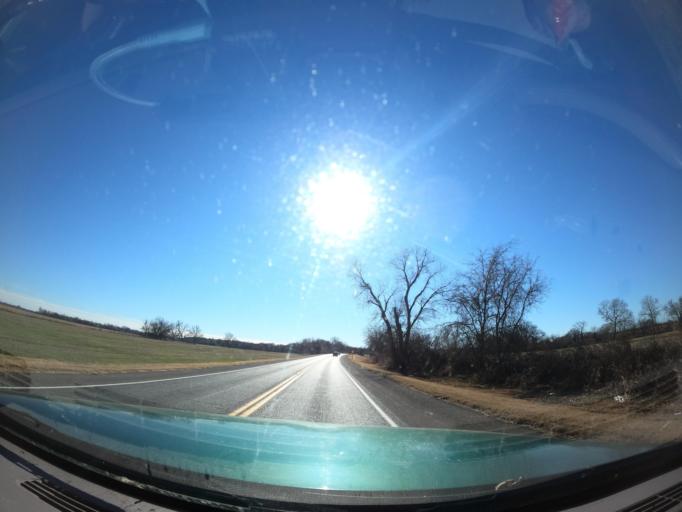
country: US
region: Oklahoma
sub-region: Muskogee County
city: Haskell
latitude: 35.8808
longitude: -95.6604
